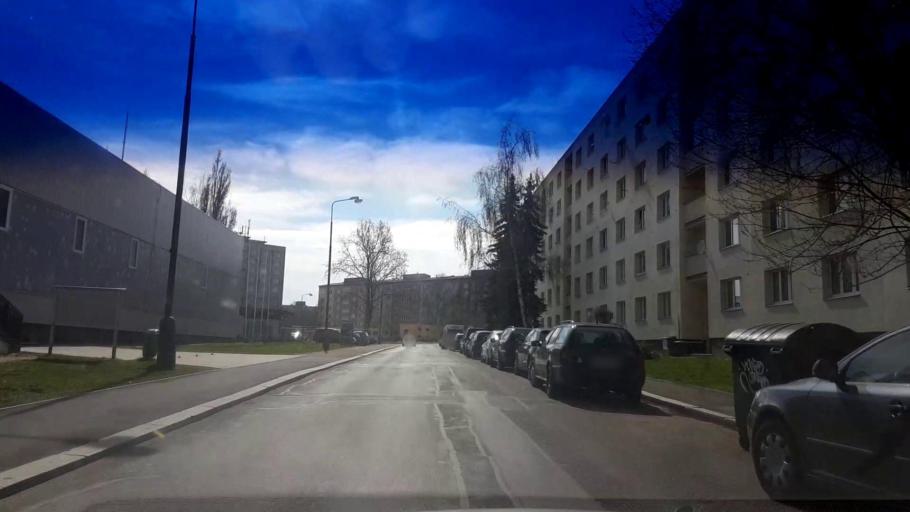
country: CZ
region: Karlovarsky
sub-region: Okres Cheb
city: Cheb
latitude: 50.0681
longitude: 12.3755
